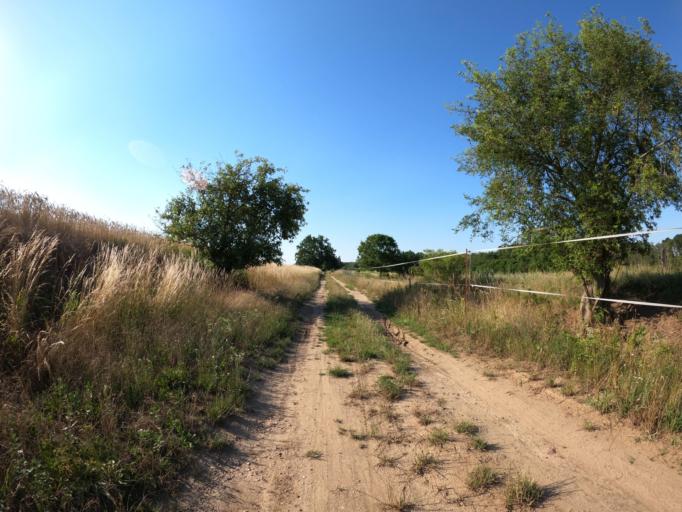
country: DE
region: Brandenburg
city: Gartz
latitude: 53.2274
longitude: 14.3690
